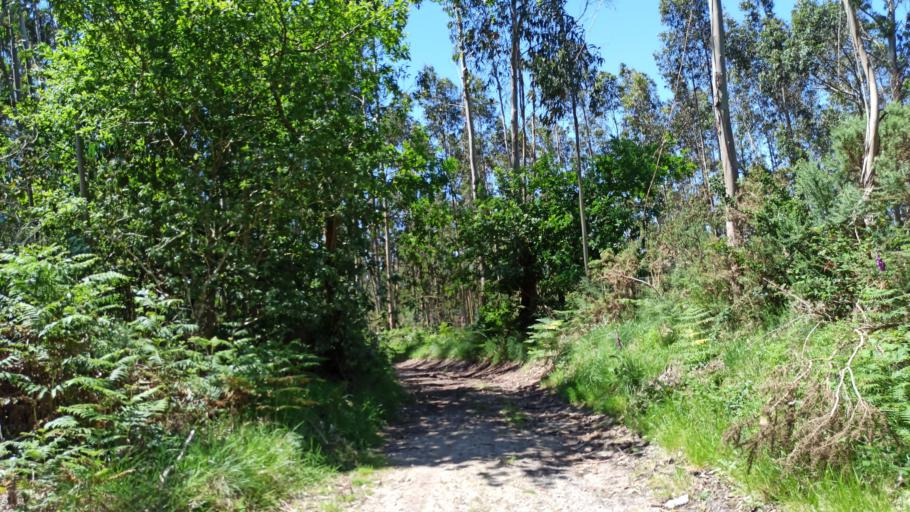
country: ES
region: Galicia
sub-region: Provincia da Coruna
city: Negreira
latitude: 42.9235
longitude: -8.7152
